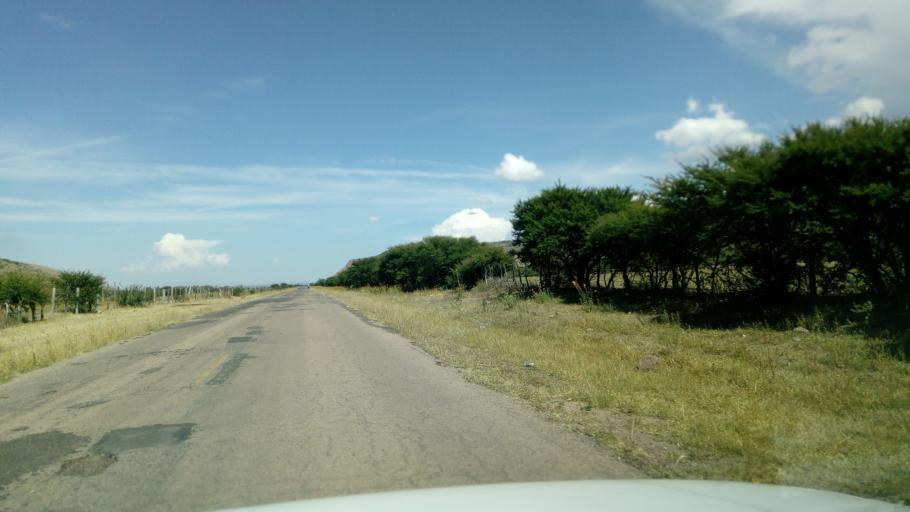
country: MX
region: Durango
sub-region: Durango
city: Jose Refugio Salcido
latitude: 23.8006
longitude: -104.4845
